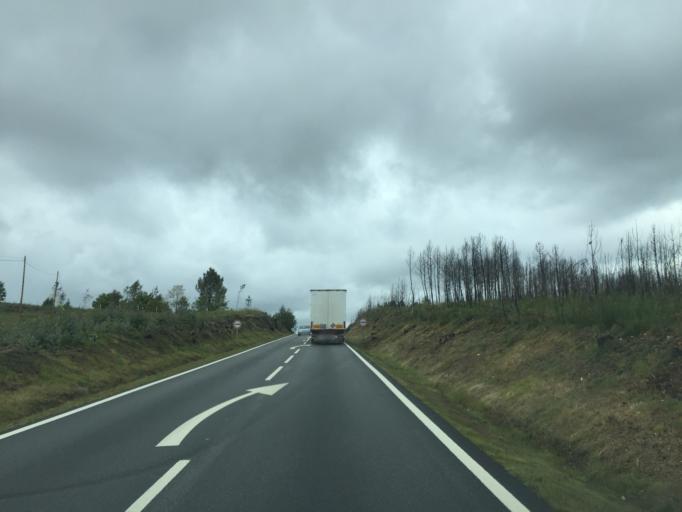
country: PT
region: Coimbra
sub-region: Oliveira do Hospital
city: Oliveira do Hospital
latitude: 40.3223
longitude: -7.9172
